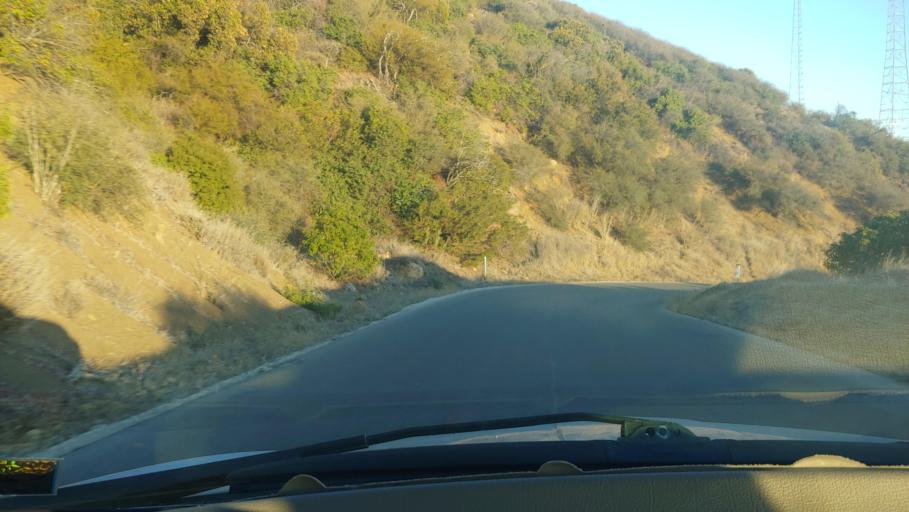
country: US
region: California
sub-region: Santa Barbara County
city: Mission Canyon
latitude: 34.4725
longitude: -119.6787
